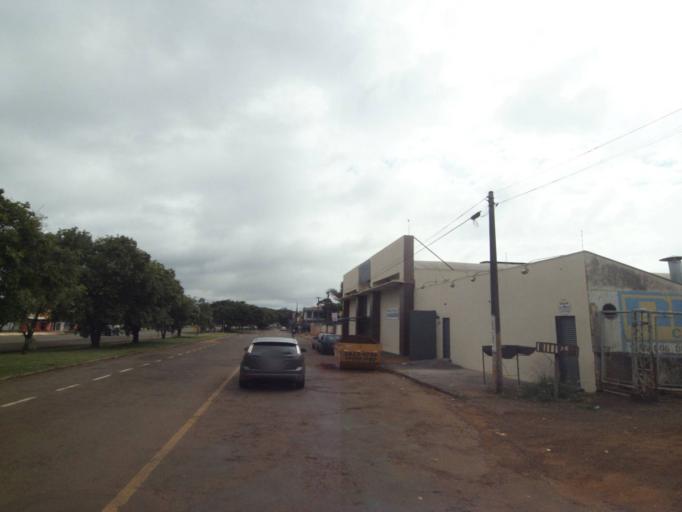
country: BR
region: Parana
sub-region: Campo Mourao
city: Campo Mourao
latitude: -24.0260
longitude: -52.3647
